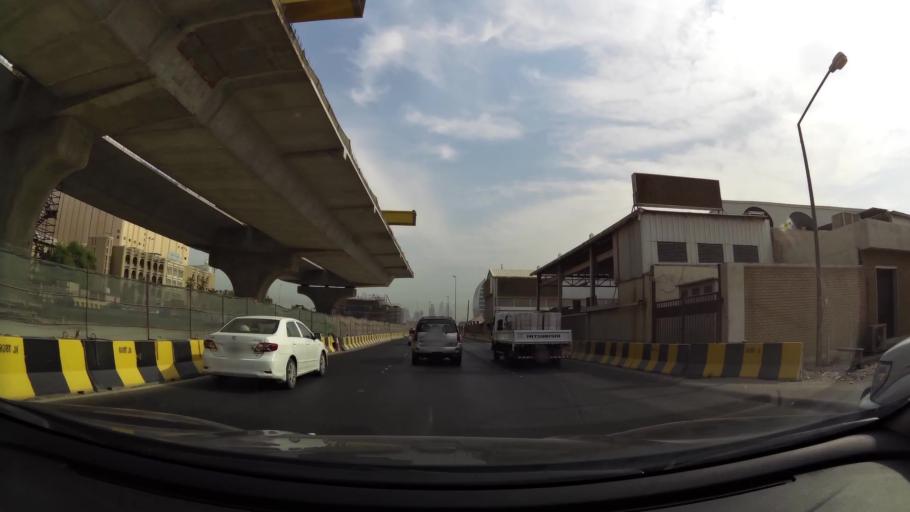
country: KW
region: Al Asimah
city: Ash Shamiyah
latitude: 29.3472
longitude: 47.9379
